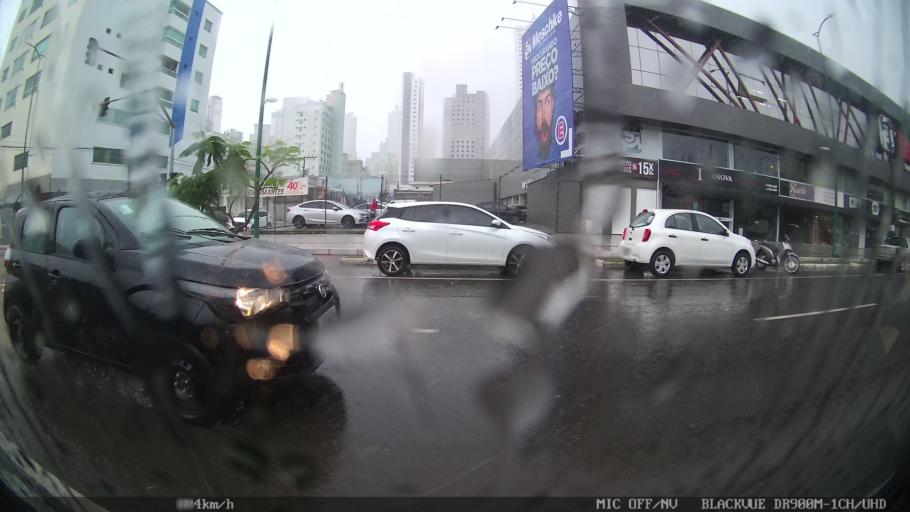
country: BR
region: Santa Catarina
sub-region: Balneario Camboriu
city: Balneario Camboriu
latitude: -26.9801
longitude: -48.6423
